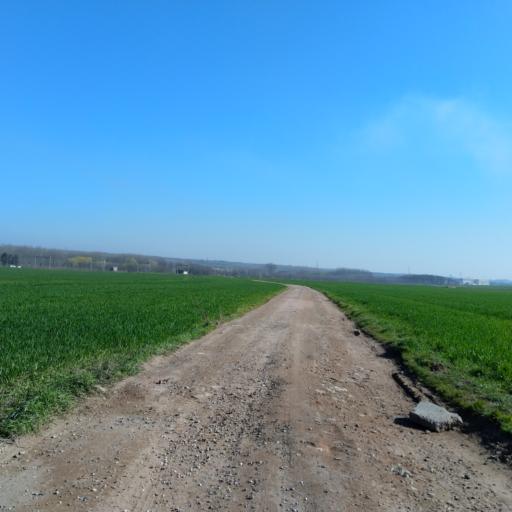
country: BE
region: Wallonia
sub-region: Province du Hainaut
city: Mons
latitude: 50.4717
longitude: 3.9638
